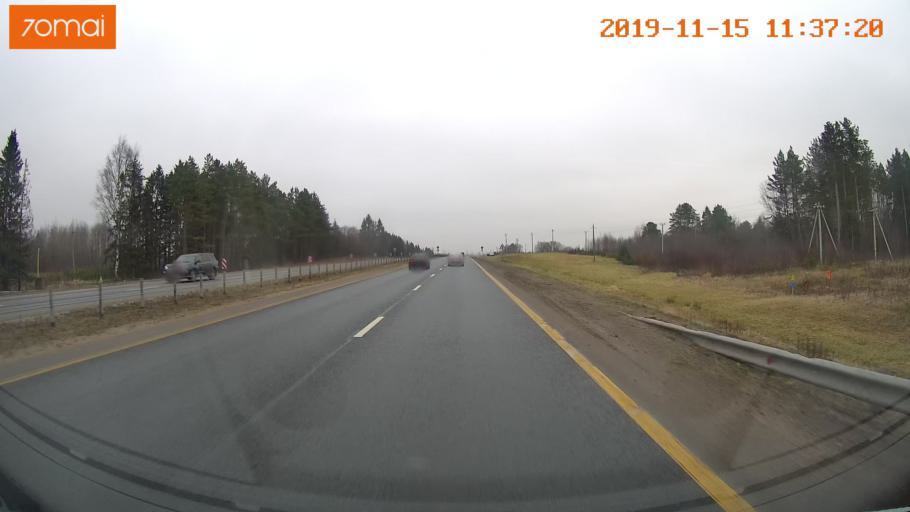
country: RU
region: Vologda
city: Molochnoye
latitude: 59.2048
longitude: 39.6697
